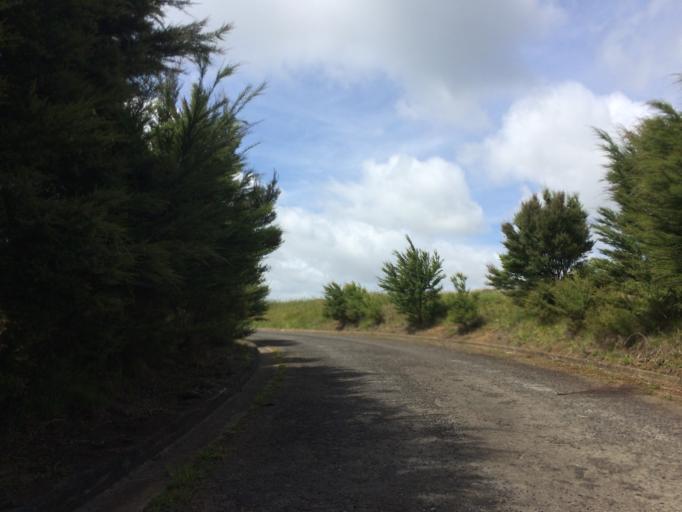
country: NZ
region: Auckland
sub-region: Auckland
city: North Shore
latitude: -36.7938
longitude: 174.6709
